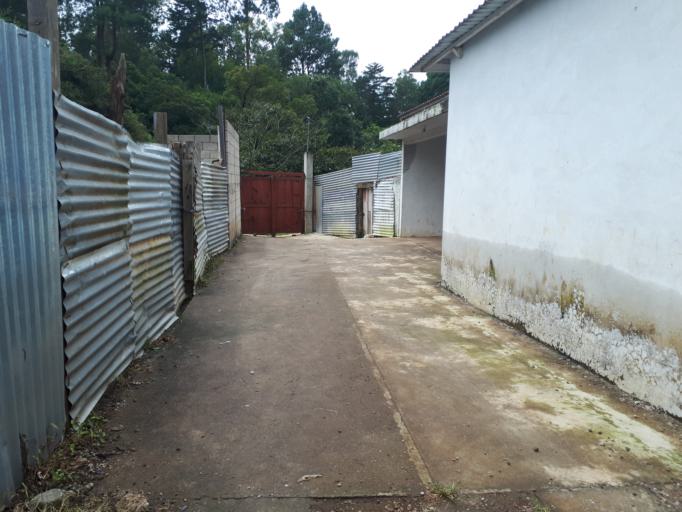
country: GT
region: Guatemala
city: Villa Canales
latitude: 14.4557
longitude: -90.5081
